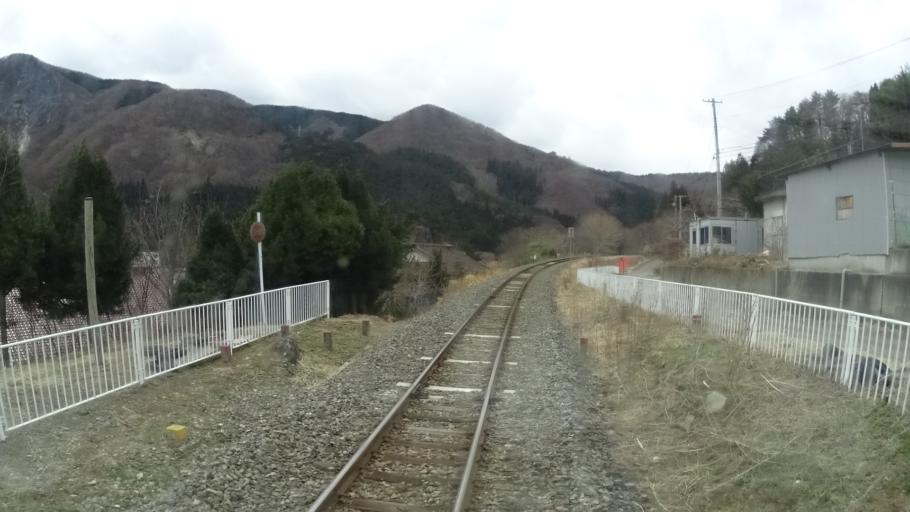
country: JP
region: Iwate
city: Kamaishi
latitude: 39.2513
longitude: 141.7650
